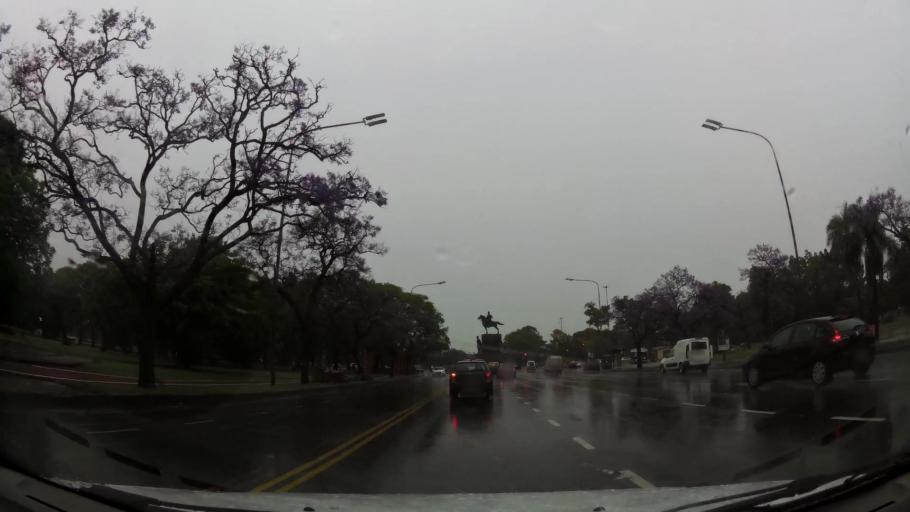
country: AR
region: Buenos Aires F.D.
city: Retiro
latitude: -34.5706
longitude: -58.4109
